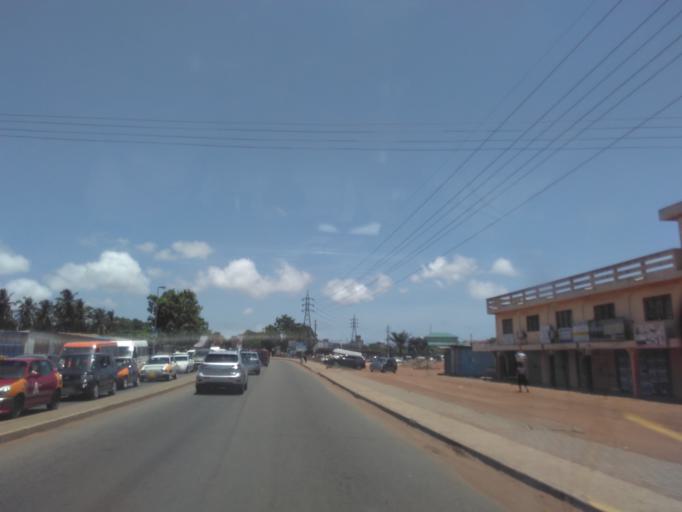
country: GH
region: Greater Accra
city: Tema
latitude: 5.6805
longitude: -0.0244
